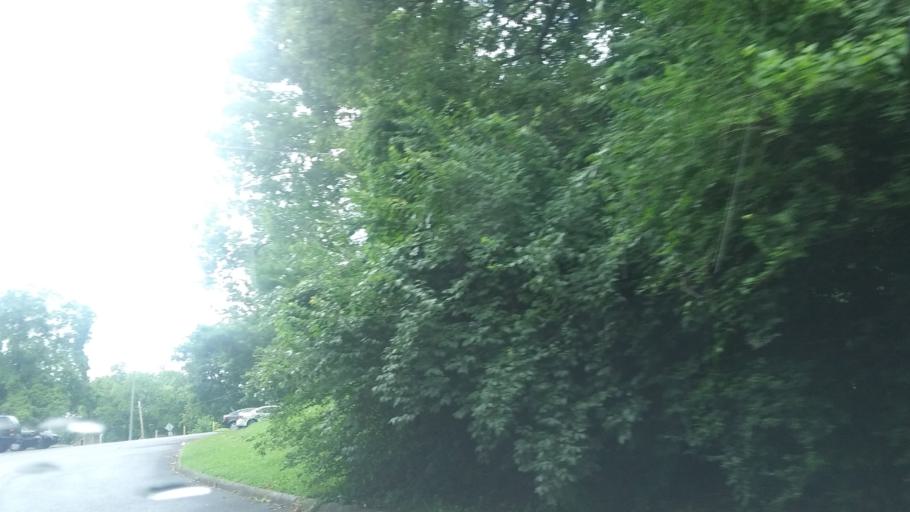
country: US
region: Tennessee
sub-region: Davidson County
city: Belle Meade
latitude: 36.1556
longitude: -86.8869
